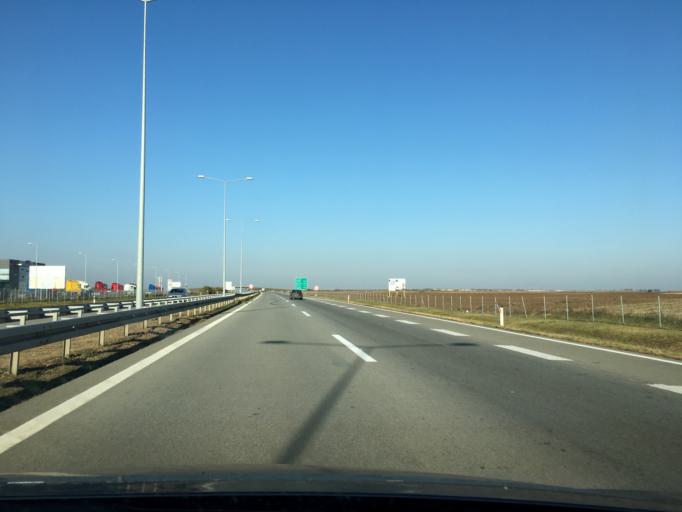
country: RS
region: Autonomna Pokrajina Vojvodina
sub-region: Juznobacki Okrug
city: Kovilj
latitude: 45.2457
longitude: 20.0295
